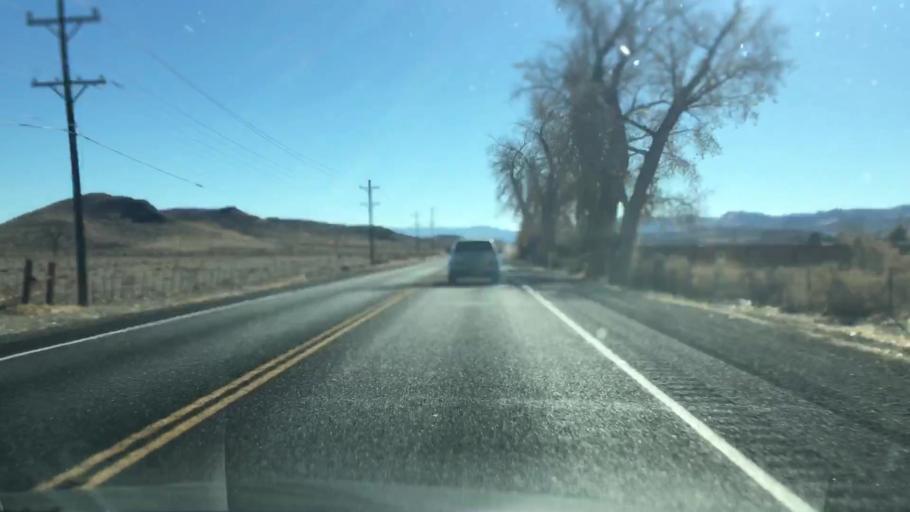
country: US
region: Nevada
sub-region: Lyon County
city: Yerington
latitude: 39.0286
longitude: -119.1816
